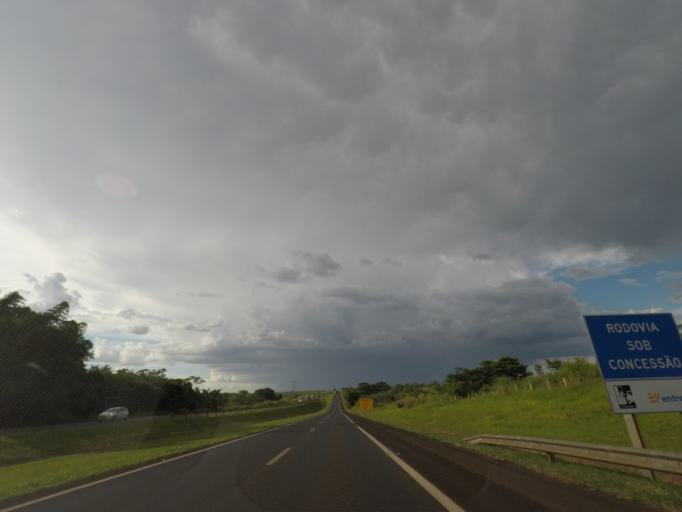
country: BR
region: Sao Paulo
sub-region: Jardinopolis
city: Jardinopolis
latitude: -21.0285
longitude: -47.8361
